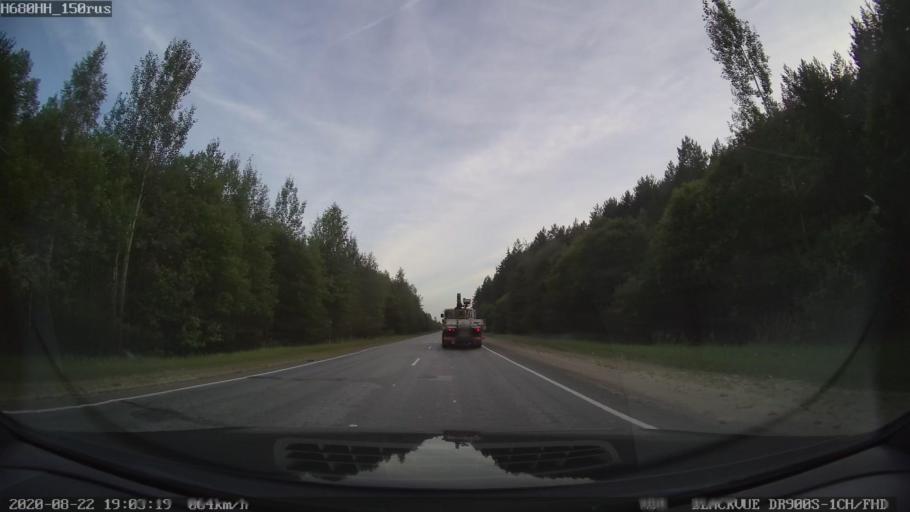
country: RU
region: Tverskaya
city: Sakharovo
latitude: 57.1001
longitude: 36.1194
